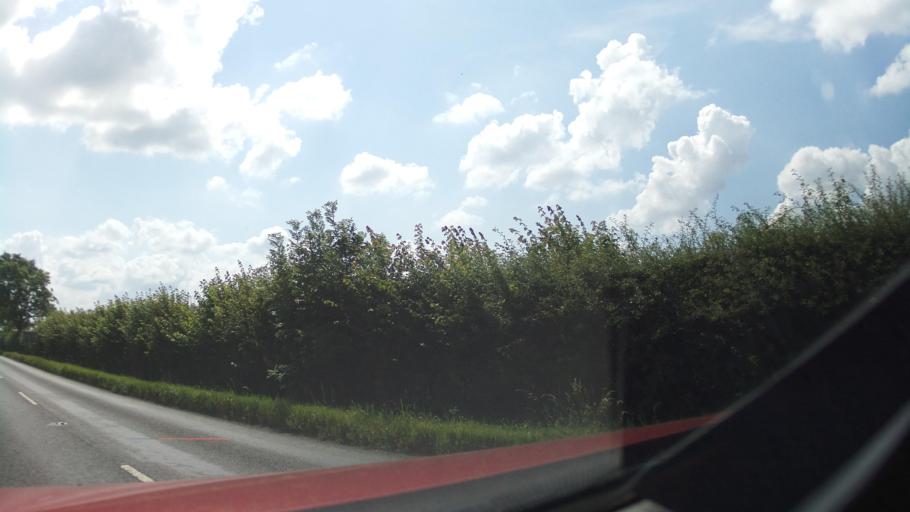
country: GB
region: England
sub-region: Wiltshire
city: Malmesbury
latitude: 51.5691
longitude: -2.0696
